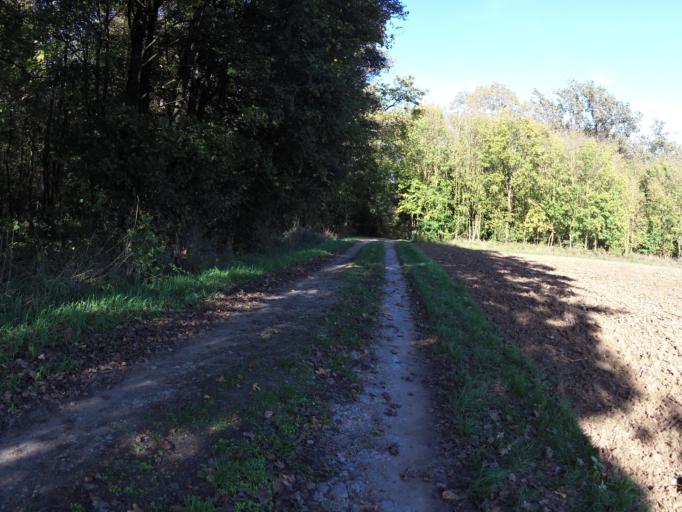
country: DE
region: Bavaria
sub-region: Regierungsbezirk Unterfranken
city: Frickenhausen
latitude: 49.7132
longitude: 10.0879
